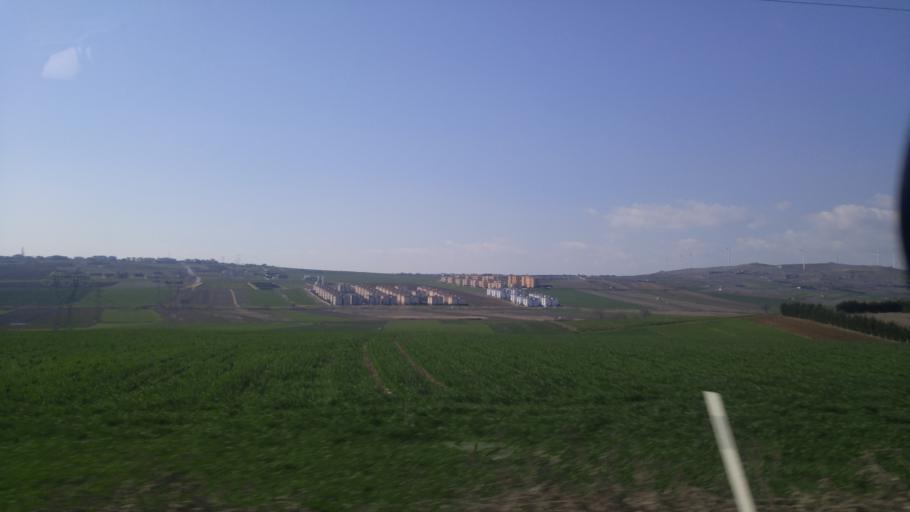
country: TR
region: Istanbul
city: Canta
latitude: 41.0904
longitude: 28.1089
